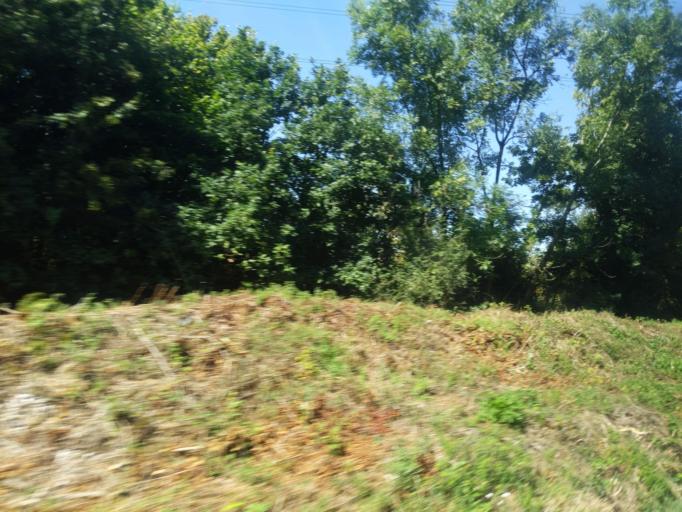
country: GB
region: England
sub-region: Devon
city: Ipplepen
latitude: 50.4822
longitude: -3.6249
